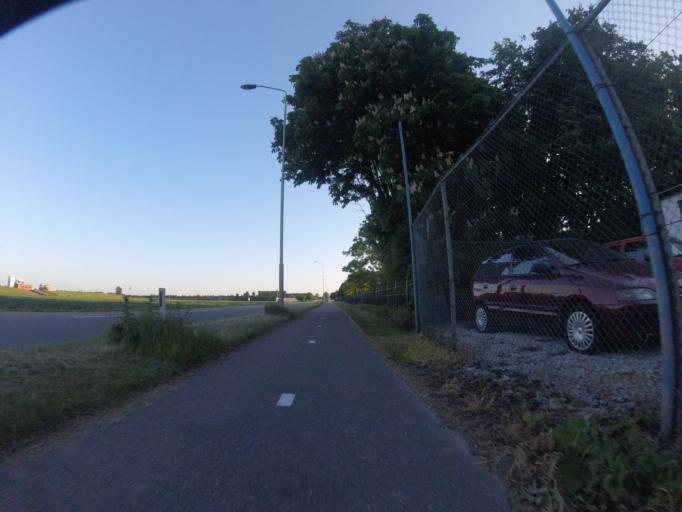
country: NL
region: North Holland
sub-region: Gemeente Haarlemmermeer
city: Hoofddorp
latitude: 52.3646
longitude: 4.7375
